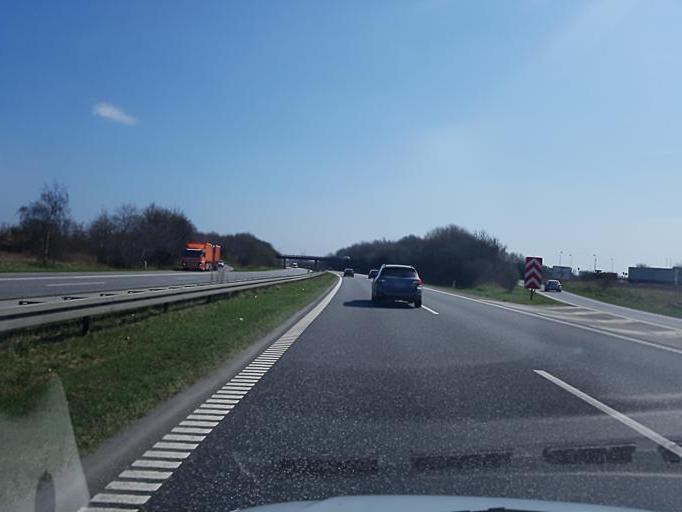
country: DK
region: South Denmark
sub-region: Fredericia Kommune
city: Taulov
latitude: 55.5390
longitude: 9.6345
